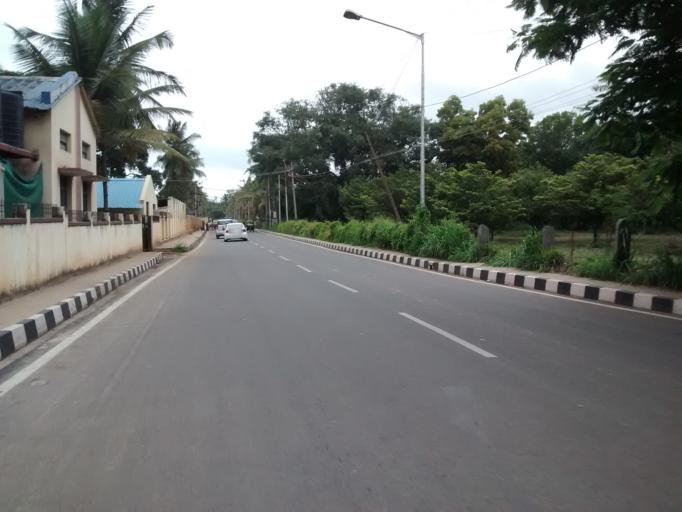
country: IN
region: Karnataka
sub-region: Bangalore Urban
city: Yelahanka
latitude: 13.0414
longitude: 77.5883
